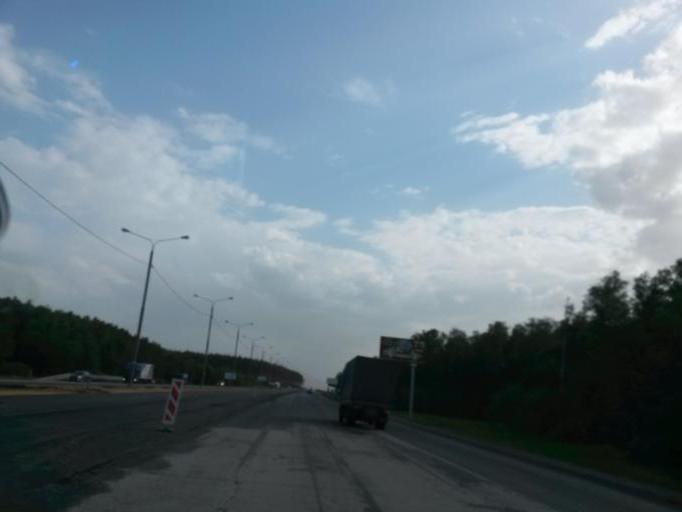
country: RU
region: Moskovskaya
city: Klimovsk
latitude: 55.3666
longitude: 37.6023
